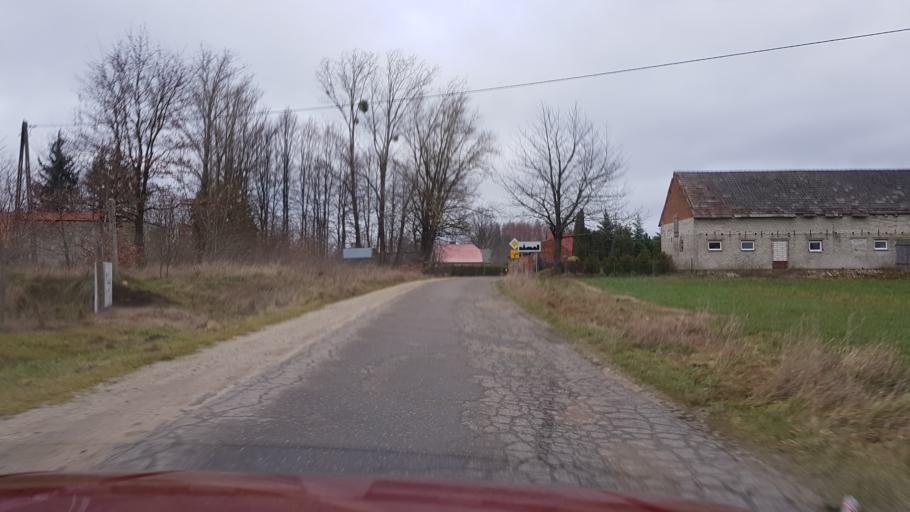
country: PL
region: Pomeranian Voivodeship
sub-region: Powiat bytowski
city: Borzytuchom
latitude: 54.1629
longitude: 17.3444
